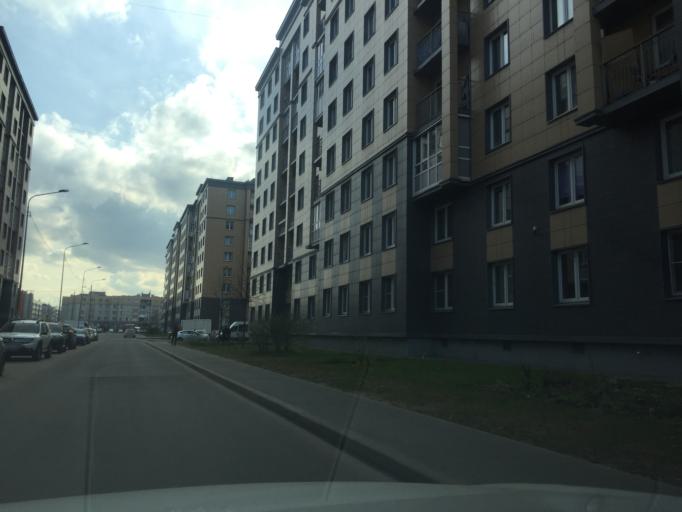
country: RU
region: St.-Petersburg
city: Tyarlevo
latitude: 59.7383
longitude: 30.4739
